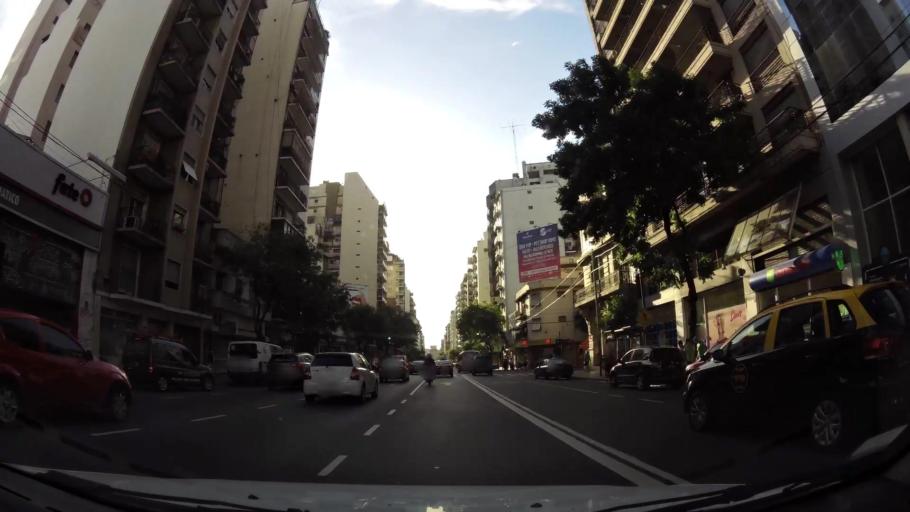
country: AR
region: Buenos Aires F.D.
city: Retiro
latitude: -34.5979
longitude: -58.4141
